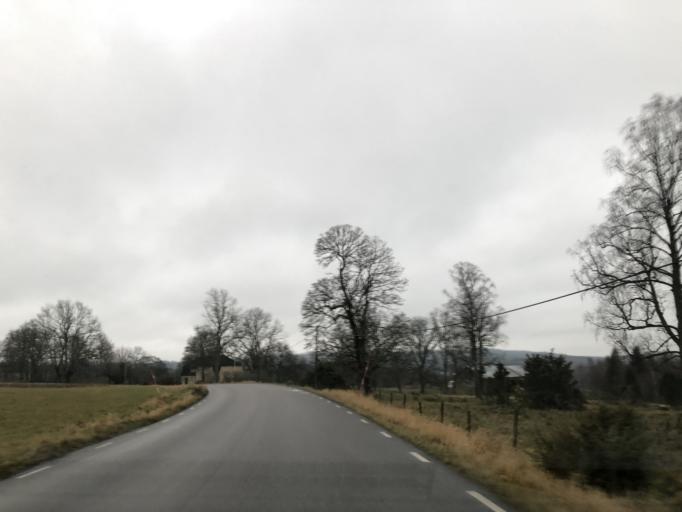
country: SE
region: Vaestra Goetaland
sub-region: Ulricehamns Kommun
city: Ulricehamn
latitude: 57.8471
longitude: 13.2627
